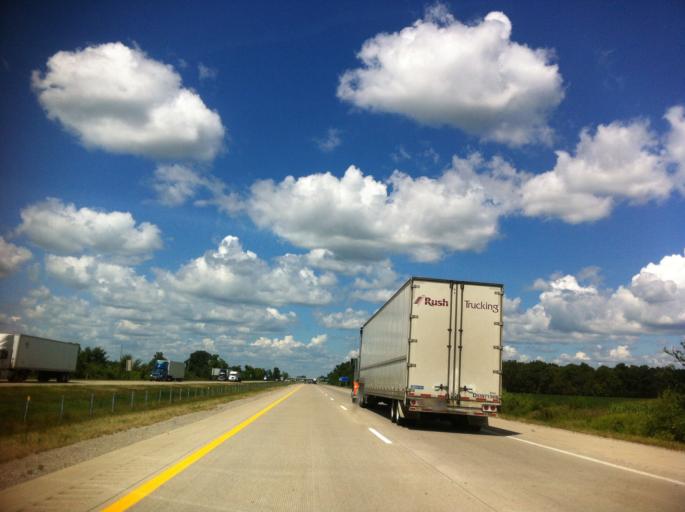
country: US
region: Ohio
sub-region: Lucas County
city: Sylvania
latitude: 41.7577
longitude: -83.6945
